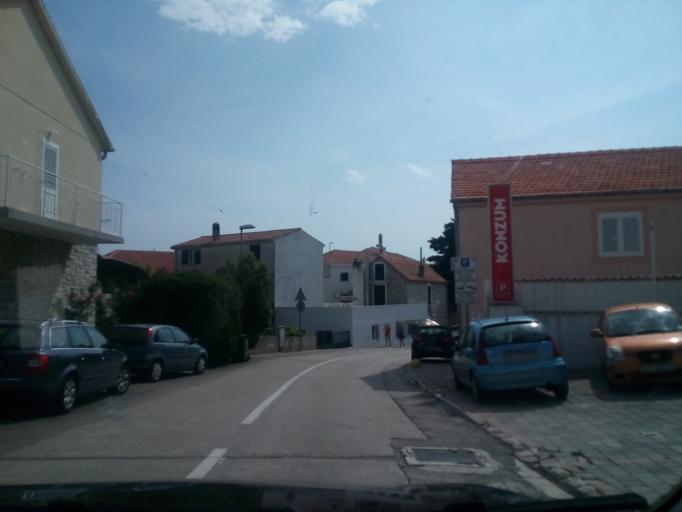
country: HR
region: Sibensko-Kniniska
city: Primosten
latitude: 43.5870
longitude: 15.9244
